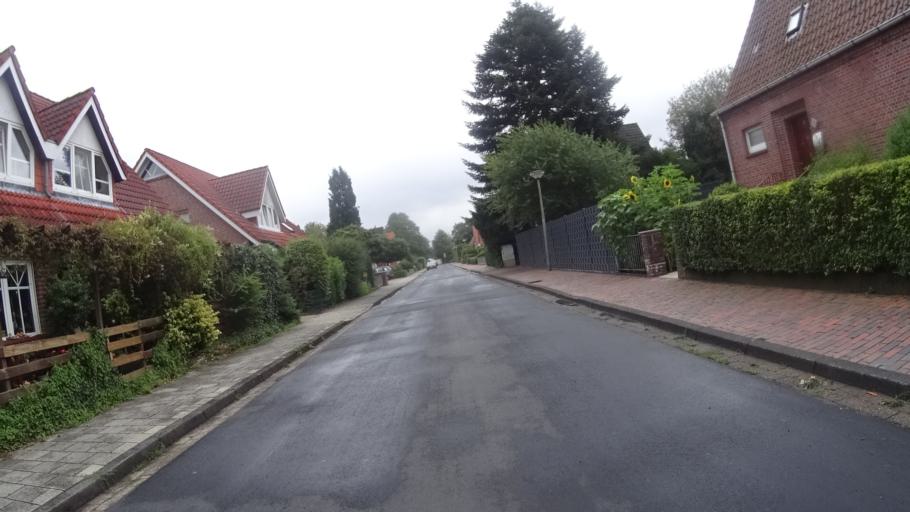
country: DE
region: Lower Saxony
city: Leer
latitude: 53.2343
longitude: 7.4453
